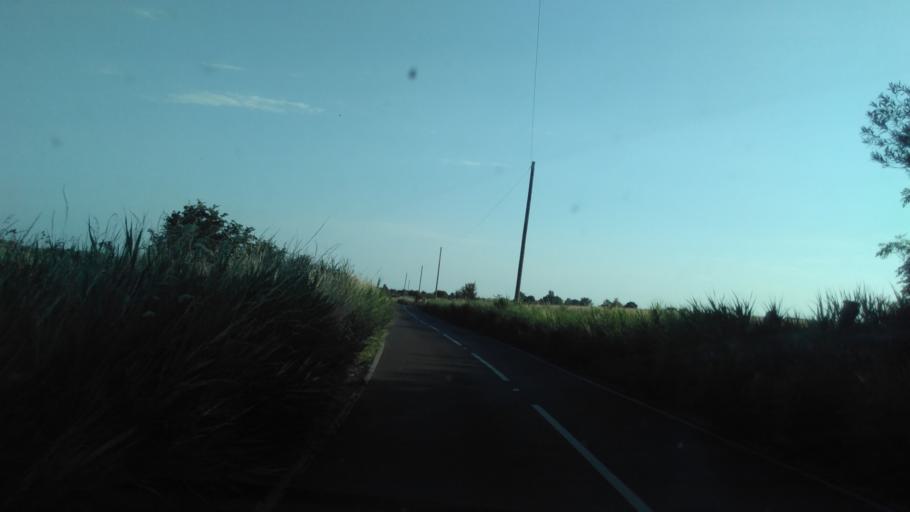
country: GB
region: England
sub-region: Kent
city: Whitstable
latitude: 51.3355
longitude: 0.9999
